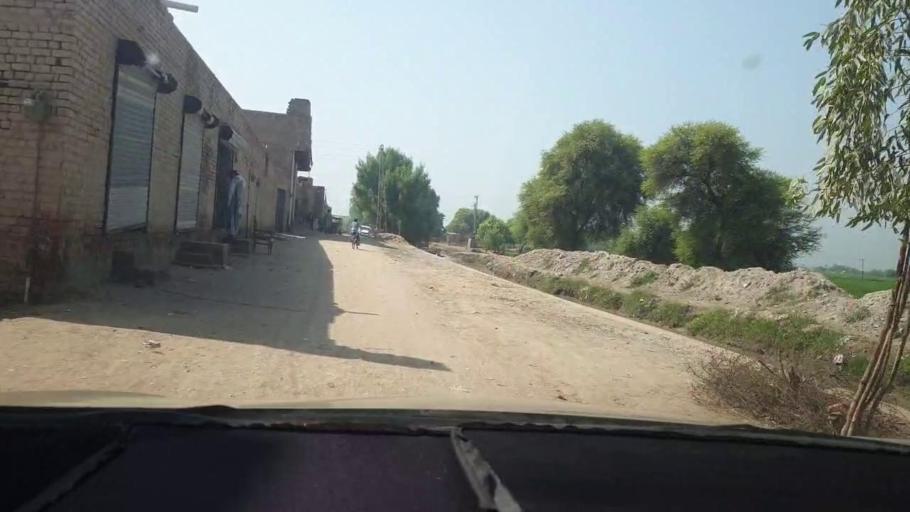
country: PK
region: Sindh
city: Kambar
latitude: 27.5702
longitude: 68.0404
